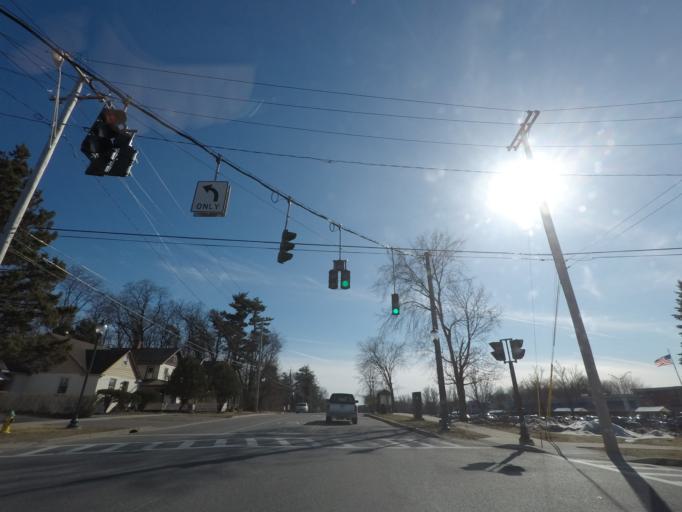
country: US
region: New York
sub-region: Saratoga County
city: Saratoga Springs
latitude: 43.0730
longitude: -73.7911
